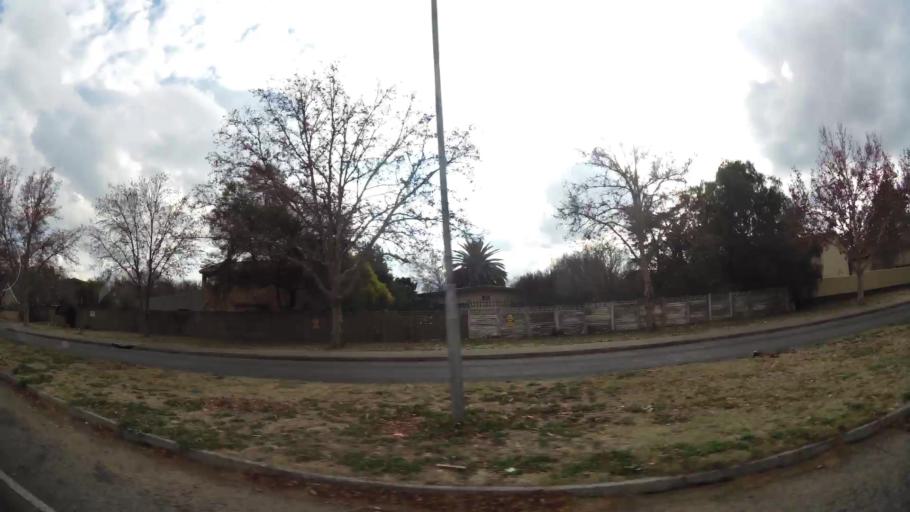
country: ZA
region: Orange Free State
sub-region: Fezile Dabi District Municipality
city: Sasolburg
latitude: -26.8086
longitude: 27.8285
